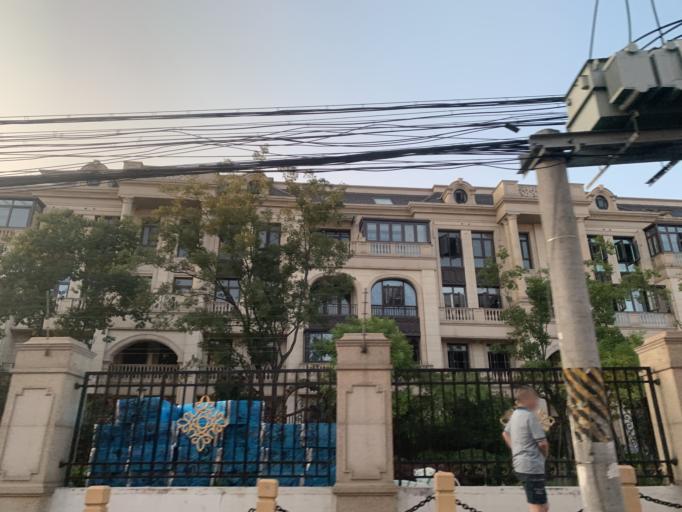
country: CN
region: Shanghai Shi
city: Huamu
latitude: 31.1870
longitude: 121.5440
